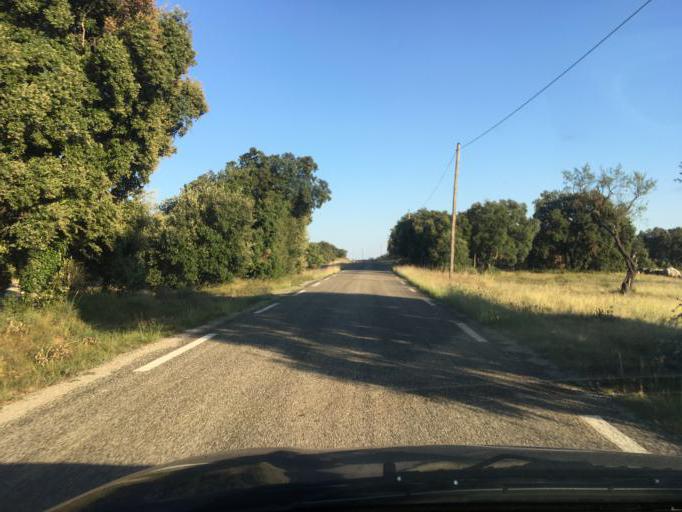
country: FR
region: Languedoc-Roussillon
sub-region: Departement du Gard
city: Saint-Victor-la-Coste
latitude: 44.0150
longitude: 4.6473
